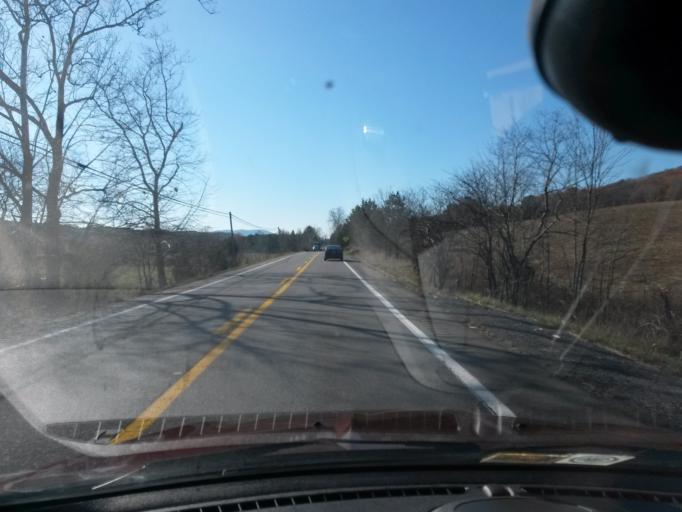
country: US
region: Virginia
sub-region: Alleghany County
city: Clifton Forge
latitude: 37.7294
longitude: -79.8022
